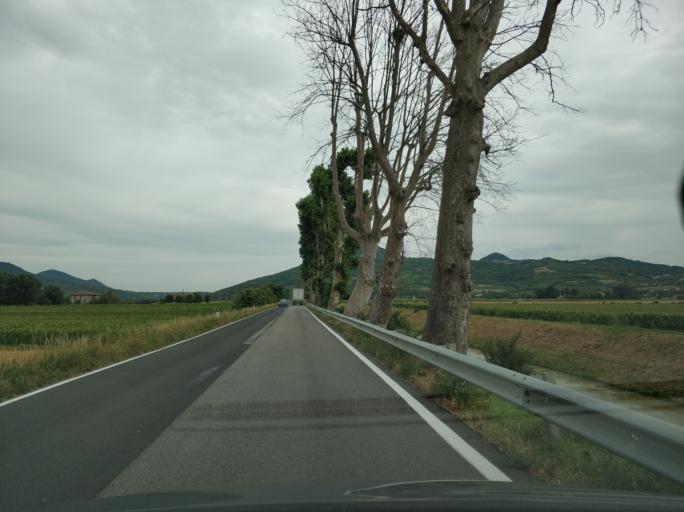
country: IT
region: Veneto
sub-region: Provincia di Padova
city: Lozzo Atestino
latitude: 45.2625
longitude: 11.6285
